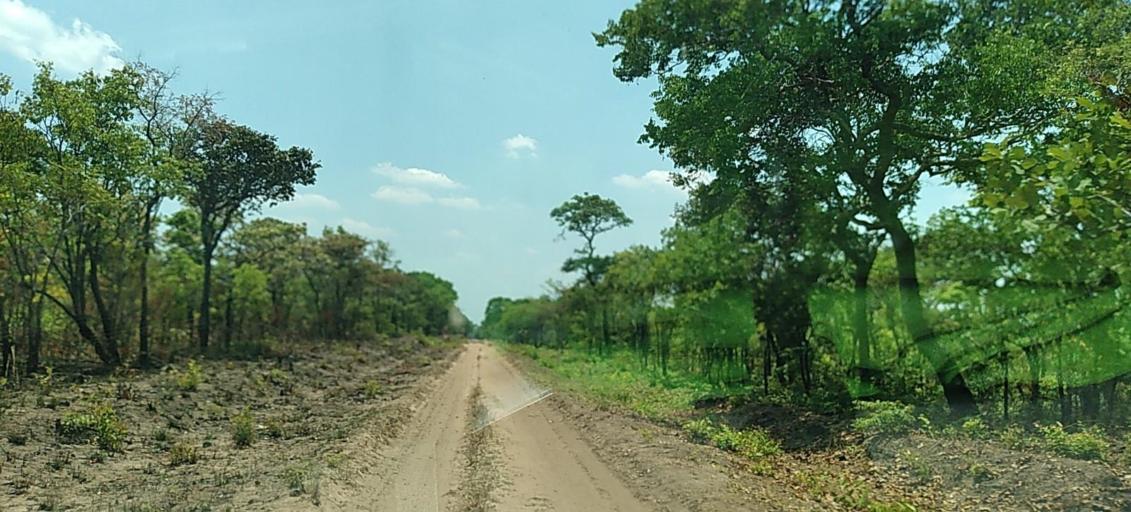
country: CD
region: Katanga
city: Kolwezi
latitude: -11.3855
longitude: 25.2198
